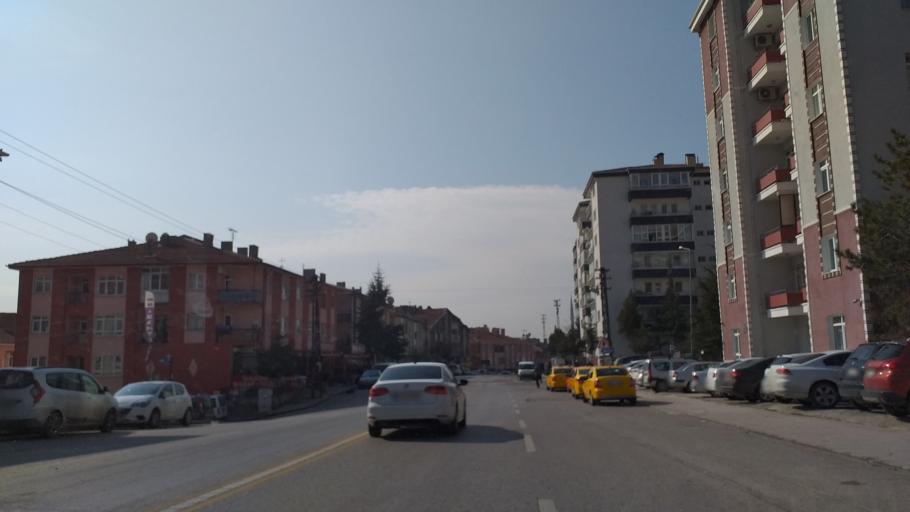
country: TR
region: Ankara
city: Ankara
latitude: 39.9903
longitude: 32.8558
